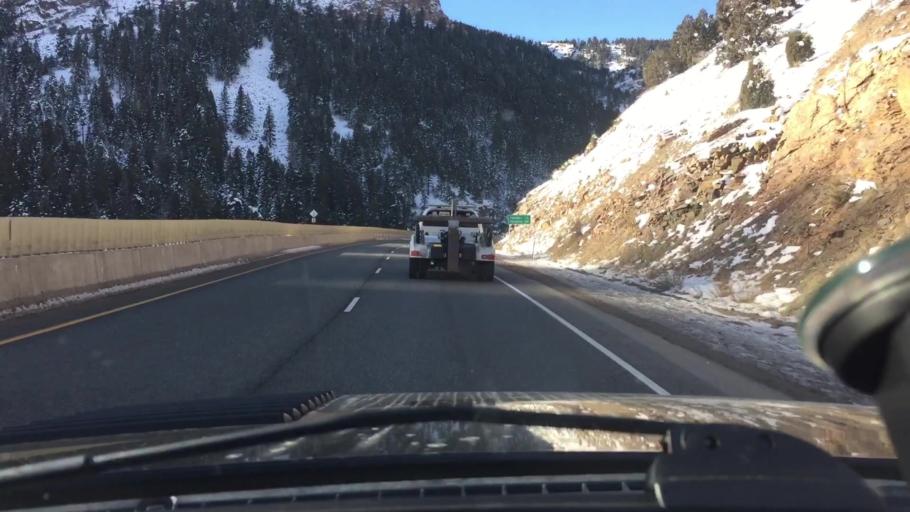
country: US
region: Colorado
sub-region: Jefferson County
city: Indian Hills
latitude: 39.6205
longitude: -105.2021
